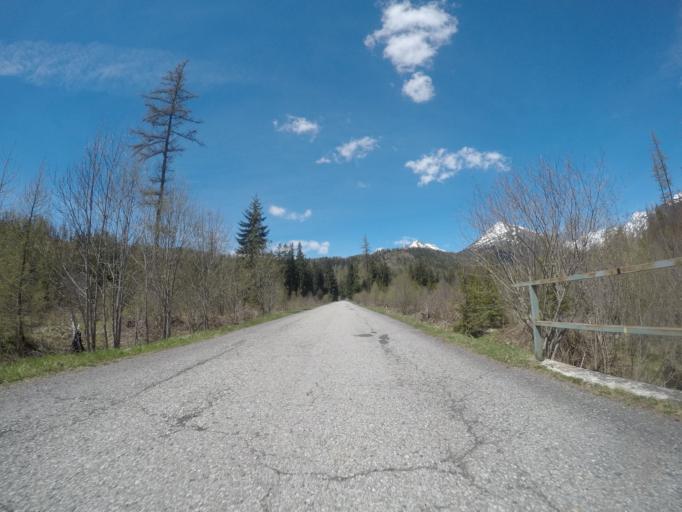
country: SK
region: Presovsky
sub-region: Okres Poprad
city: Strba
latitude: 49.1184
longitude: 20.0782
